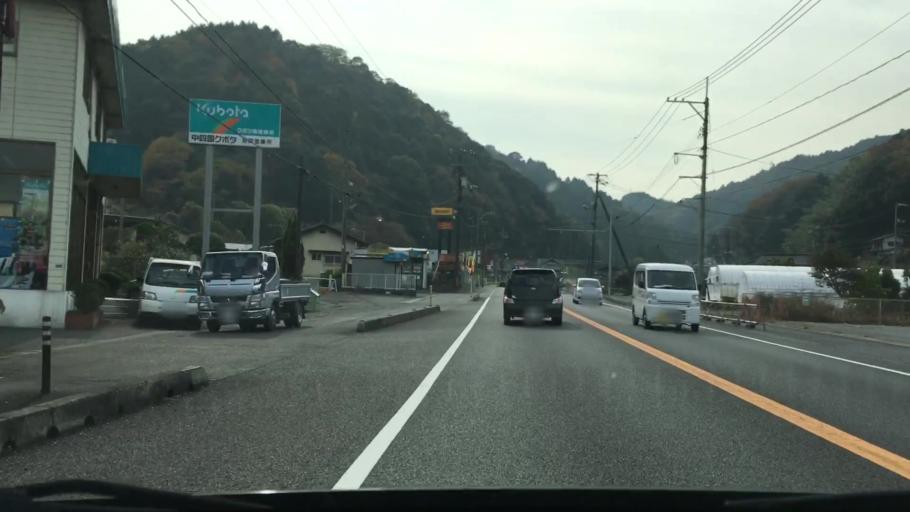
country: JP
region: Yamaguchi
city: Iwakuni
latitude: 34.1549
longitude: 132.1749
